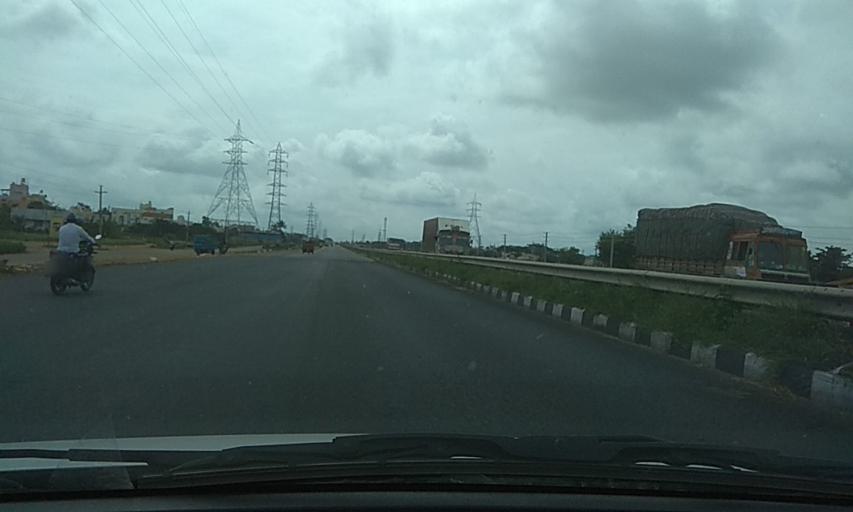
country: IN
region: Karnataka
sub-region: Davanagere
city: Harihar
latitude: 14.4362
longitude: 75.9111
